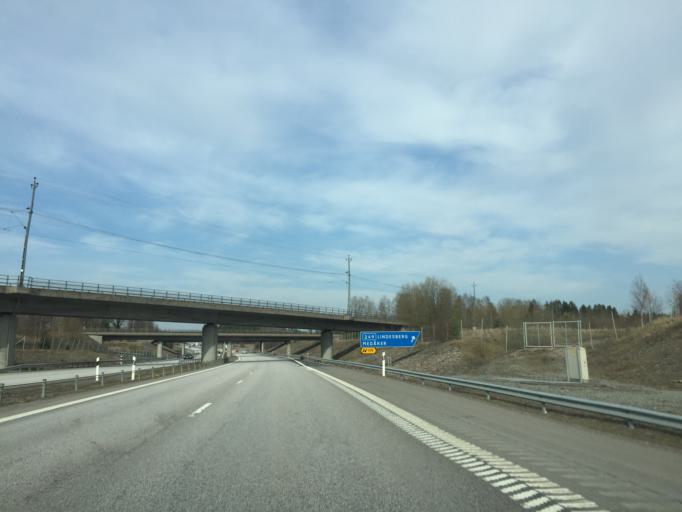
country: SE
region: Vaestmanland
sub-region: Arboga Kommun
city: Arboga
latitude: 59.4101
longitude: 15.7661
